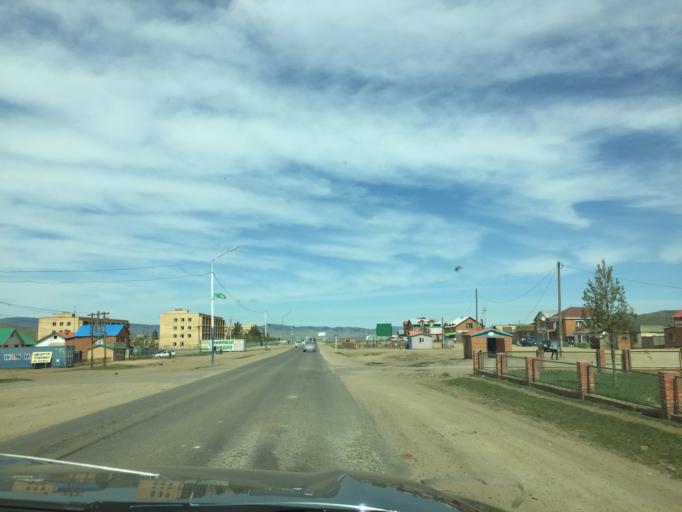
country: MN
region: Central Aimak
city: Ihsueuej
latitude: 48.2245
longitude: 106.2932
